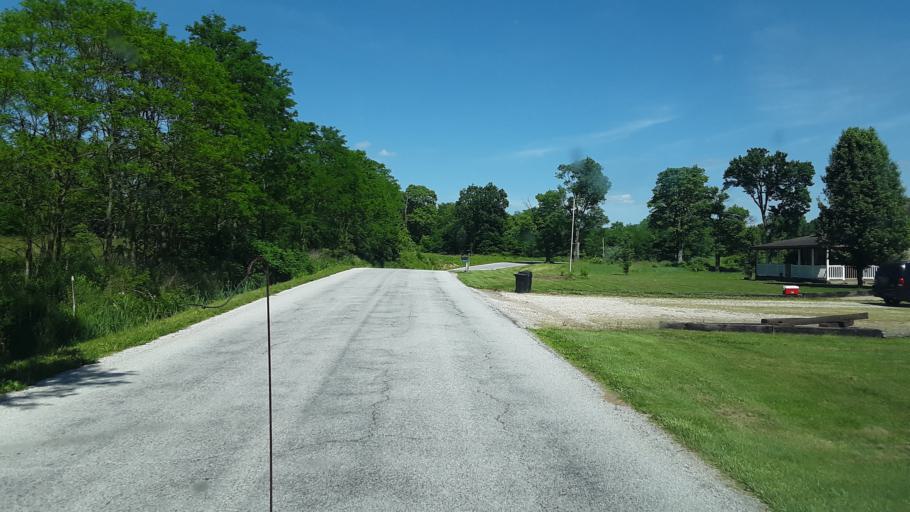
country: US
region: Ohio
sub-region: Coshocton County
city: Coshocton
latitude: 40.2303
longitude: -81.8319
